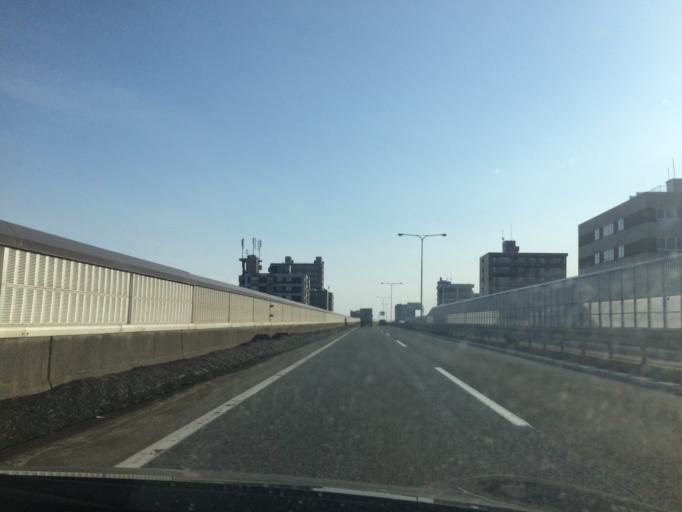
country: JP
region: Hokkaido
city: Sapporo
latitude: 43.1039
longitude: 141.3642
